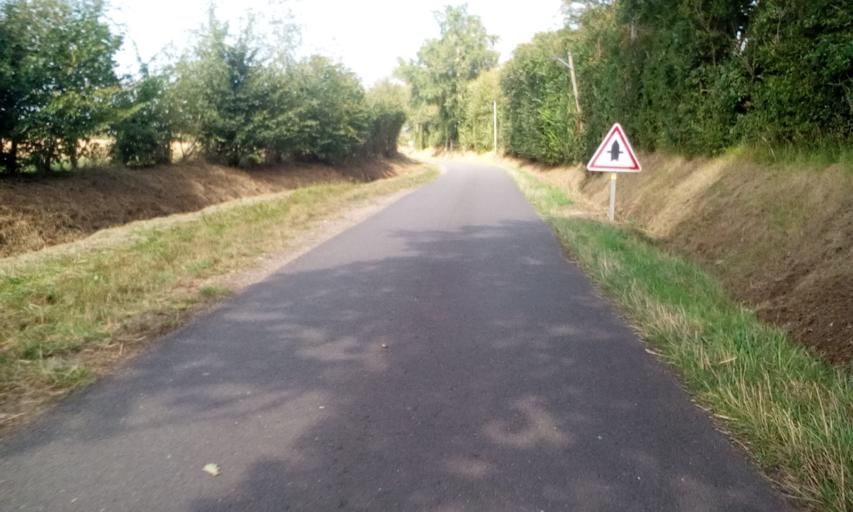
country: FR
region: Lower Normandy
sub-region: Departement du Calvados
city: Argences
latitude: 49.1490
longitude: -0.1250
